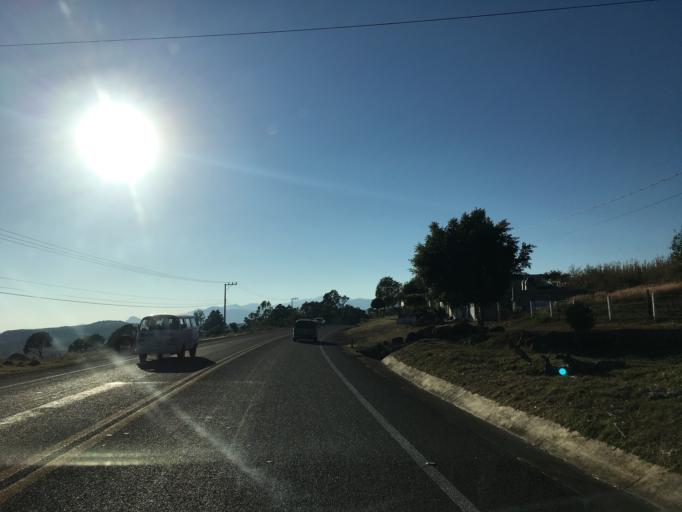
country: MX
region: Michoacan
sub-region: Zitacuaro
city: Puentecillas (Tercera Manzana de Zirahuato)
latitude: 19.4795
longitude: -100.4292
